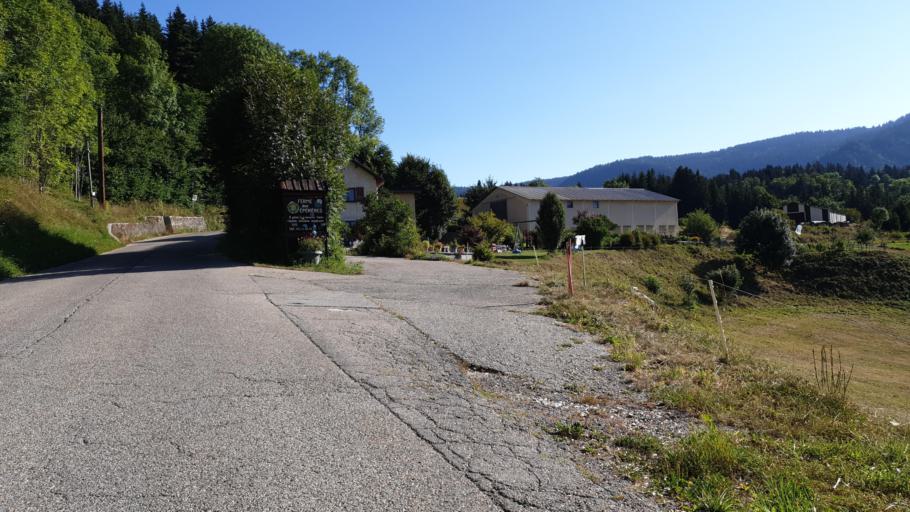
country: FR
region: Rhone-Alpes
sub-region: Departement de l'Isere
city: Autrans
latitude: 45.1871
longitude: 5.5473
